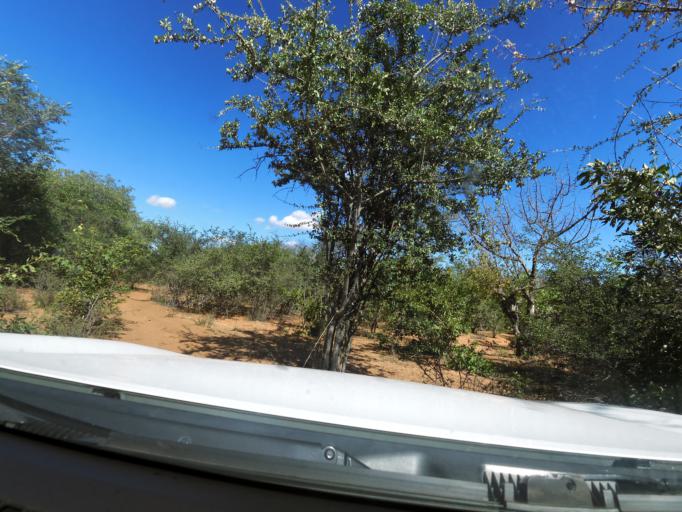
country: ZW
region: Matabeleland North
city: Kamativi Mine
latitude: -17.9653
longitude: 27.1424
